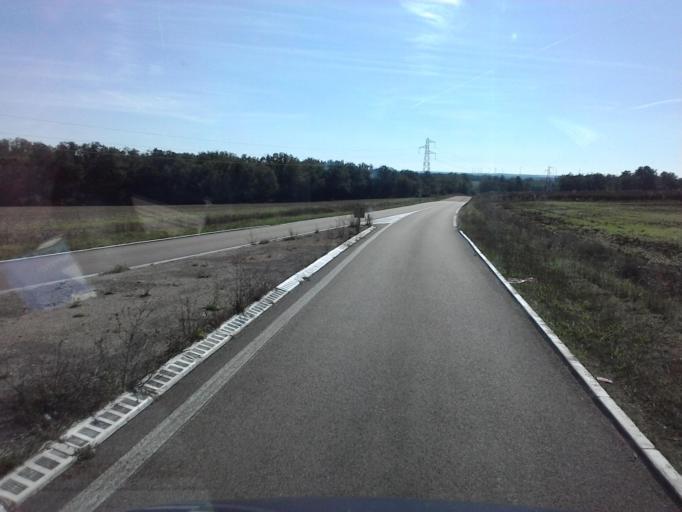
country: FR
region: Bourgogne
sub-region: Departement de l'Yonne
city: Joux-la-Ville
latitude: 47.7174
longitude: 3.9099
